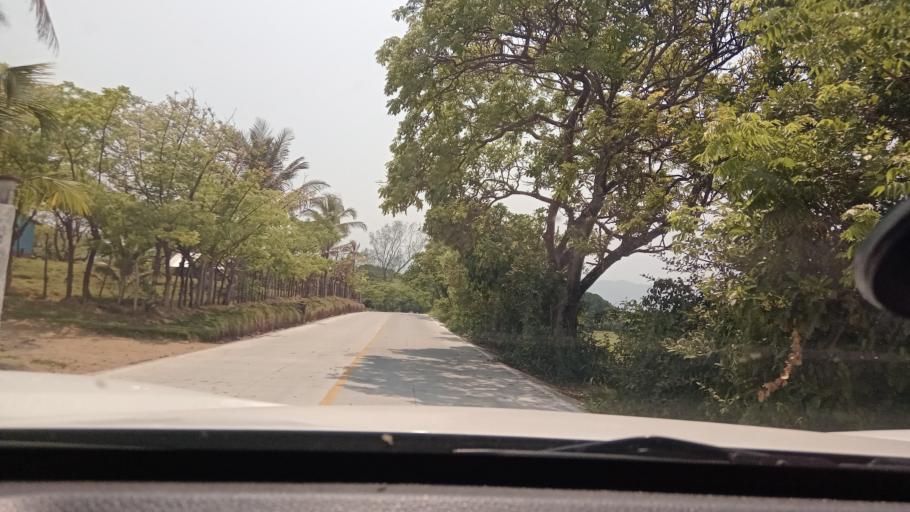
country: MX
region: Veracruz
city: Catemaco
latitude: 18.5578
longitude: -95.0116
